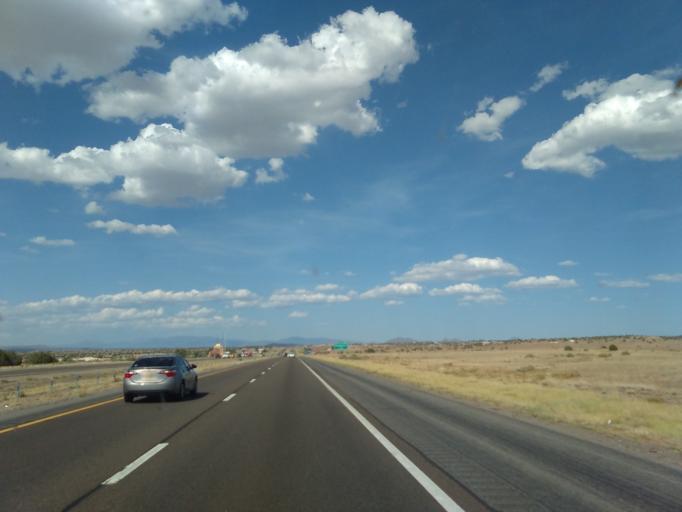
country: US
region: New Mexico
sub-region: Sandoval County
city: Santo Domingo Pueblo
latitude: 35.4500
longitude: -106.3535
